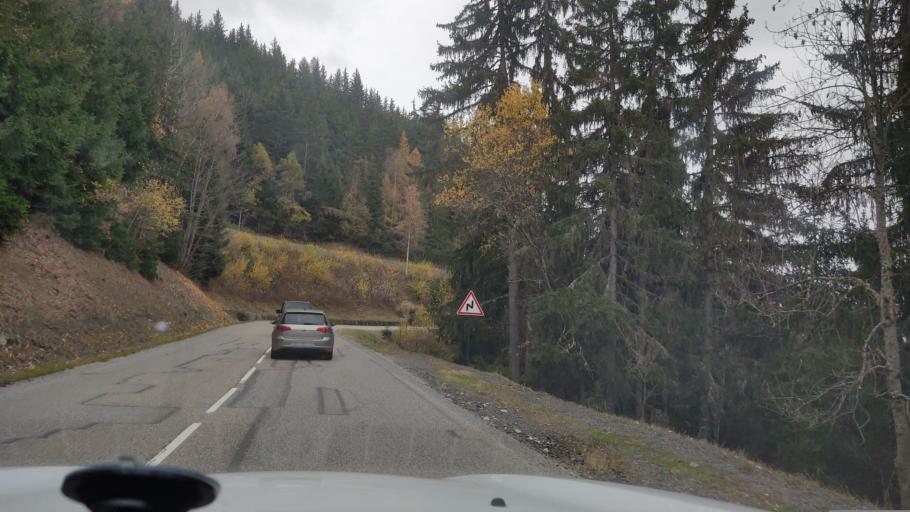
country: FR
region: Rhone-Alpes
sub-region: Departement de la Savoie
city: Bourg-Saint-Maurice
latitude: 45.5822
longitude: 6.7752
